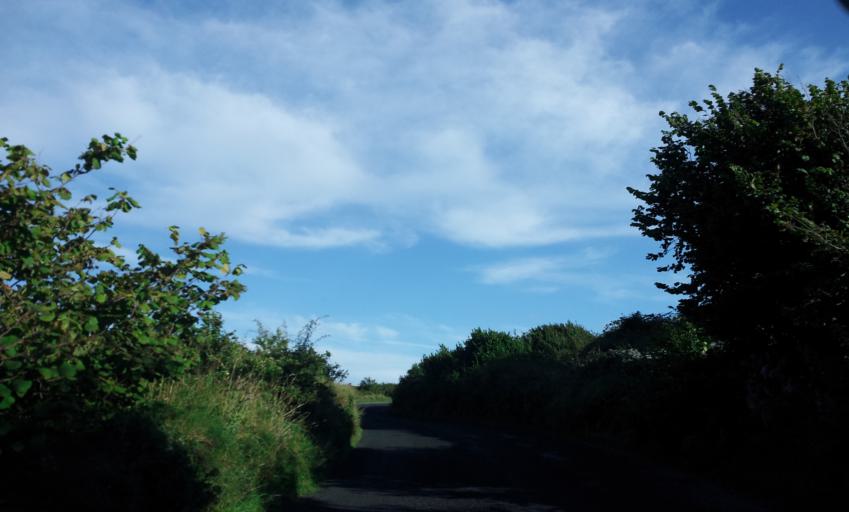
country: IE
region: Connaught
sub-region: County Galway
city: Bearna
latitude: 53.0318
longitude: -9.1355
